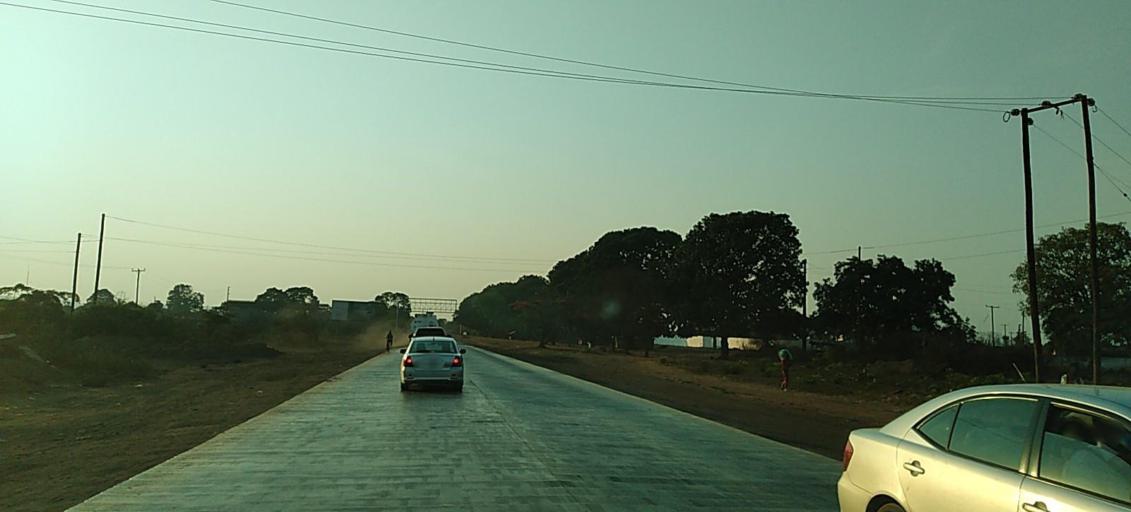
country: ZM
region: Copperbelt
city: Ndola
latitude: -13.0345
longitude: 28.6891
